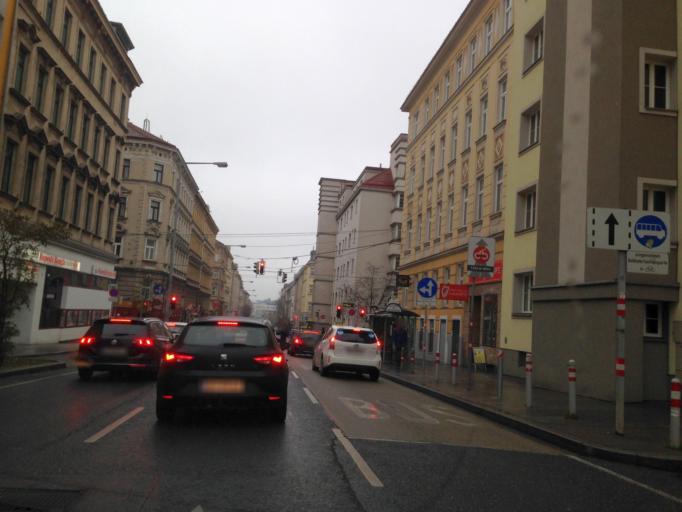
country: AT
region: Vienna
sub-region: Wien Stadt
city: Vienna
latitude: 48.2051
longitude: 16.3265
